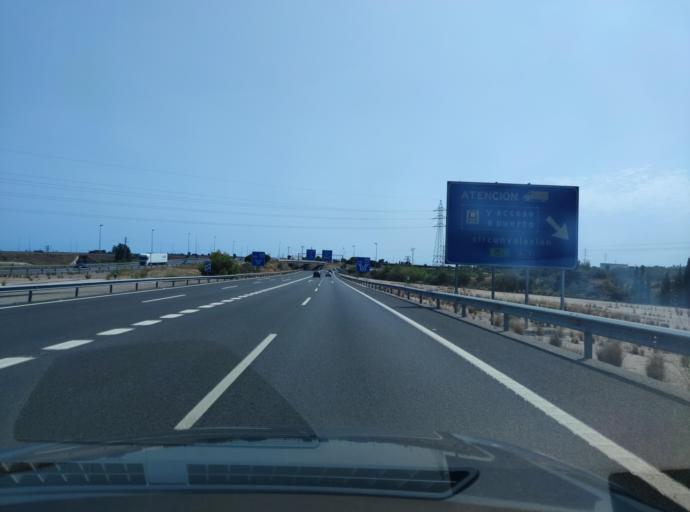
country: ES
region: Valencia
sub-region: Provincia de Valencia
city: Pucol
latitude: 39.6374
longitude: -0.3033
